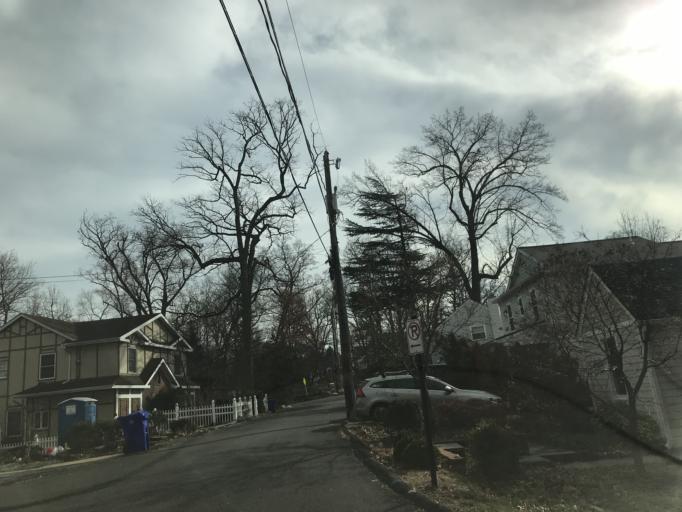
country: US
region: Virginia
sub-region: Arlington County
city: Arlington
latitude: 38.9015
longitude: -77.0980
